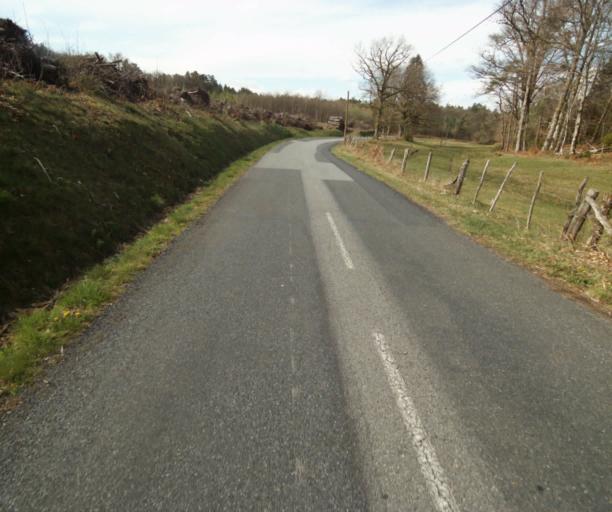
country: FR
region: Limousin
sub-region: Departement de la Correze
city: Correze
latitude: 45.3514
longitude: 1.9047
